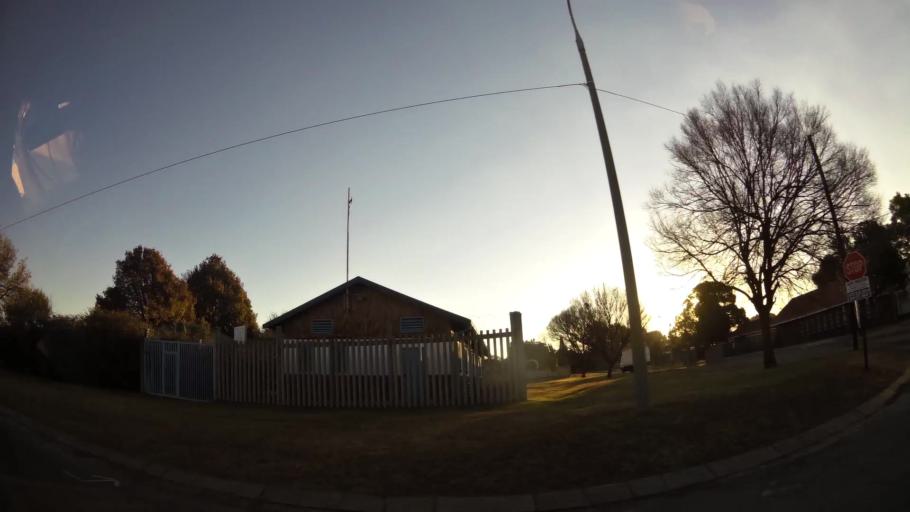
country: ZA
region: Gauteng
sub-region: City of Johannesburg Metropolitan Municipality
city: Roodepoort
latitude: -26.1505
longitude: 27.8847
